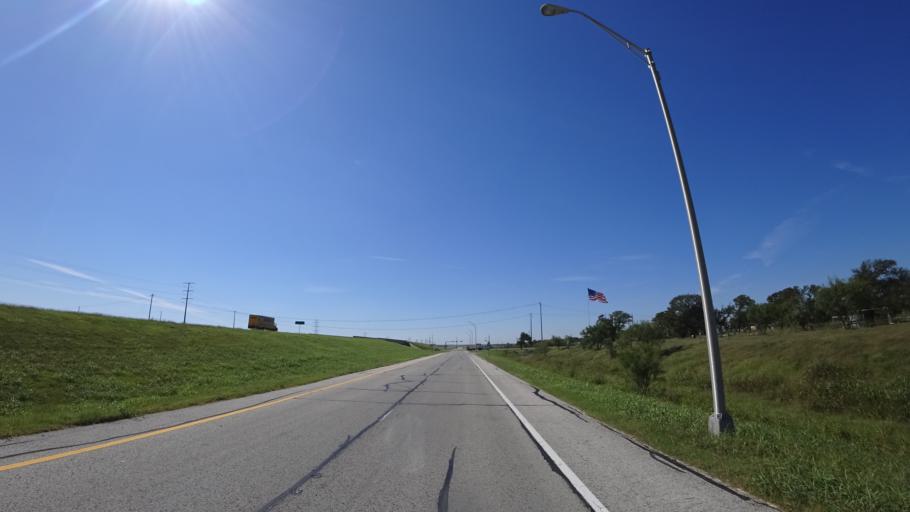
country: US
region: Texas
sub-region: Travis County
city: Hornsby Bend
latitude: 30.2560
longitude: -97.6037
